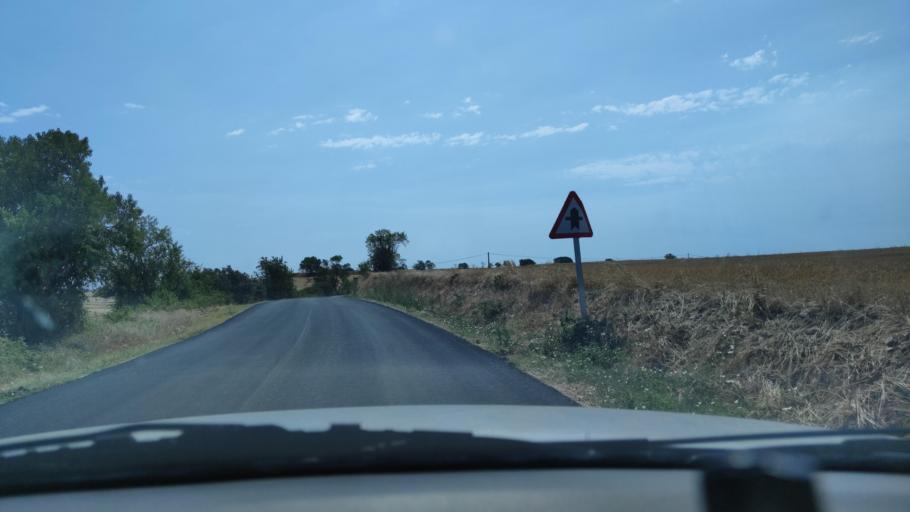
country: ES
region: Catalonia
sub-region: Provincia de Lleida
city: Ivorra
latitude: 41.7769
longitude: 1.3233
